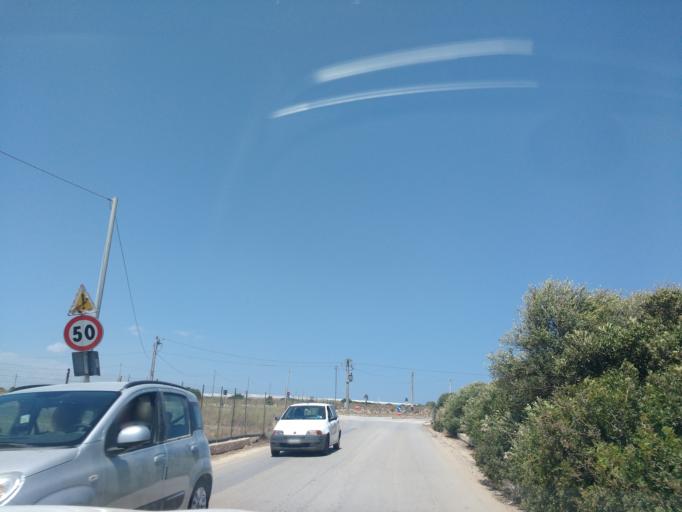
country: IT
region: Sicily
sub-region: Provincia di Siracusa
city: Pachino
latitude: 36.6738
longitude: 15.0856
